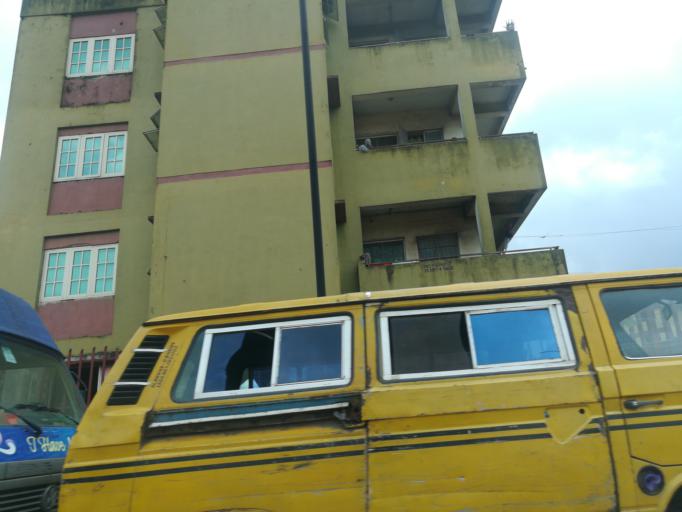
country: NG
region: Lagos
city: Mushin
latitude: 6.5315
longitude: 3.3571
